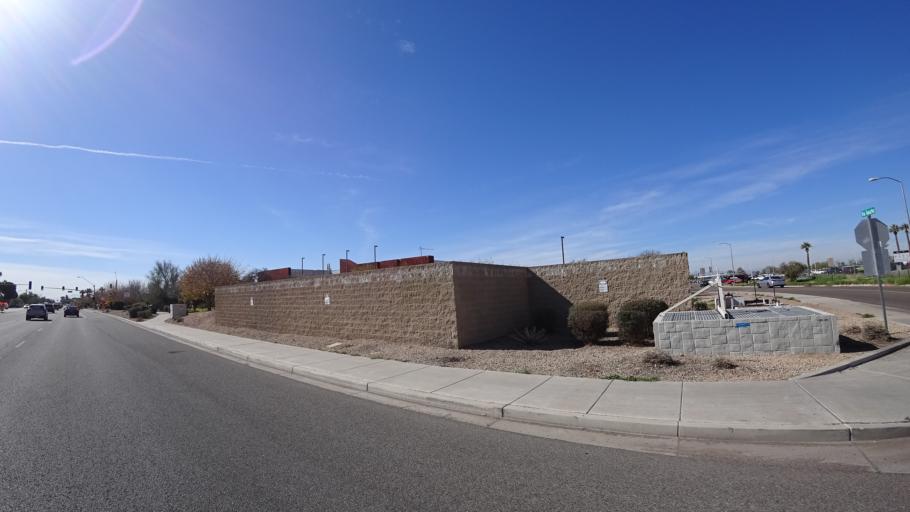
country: US
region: Arizona
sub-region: Maricopa County
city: Glendale
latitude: 33.5729
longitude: -112.1864
